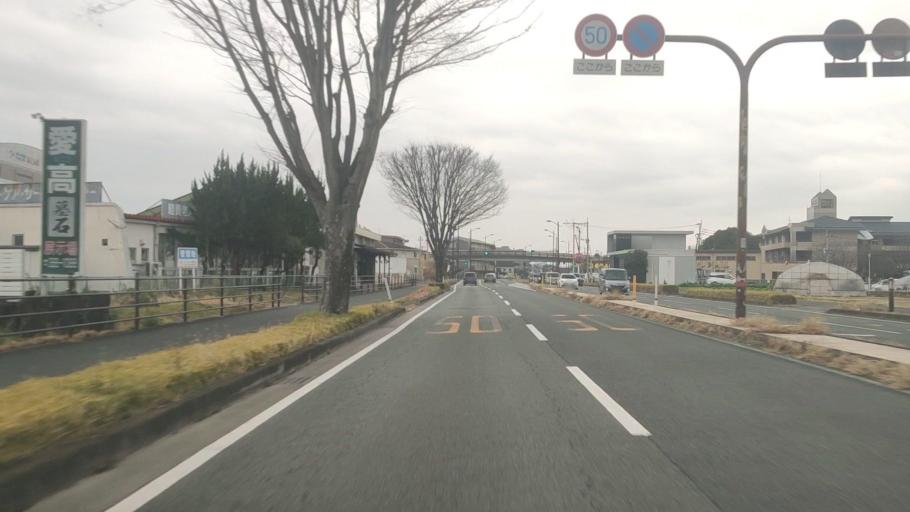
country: JP
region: Kumamoto
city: Kumamoto
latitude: 32.8130
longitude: 130.7821
